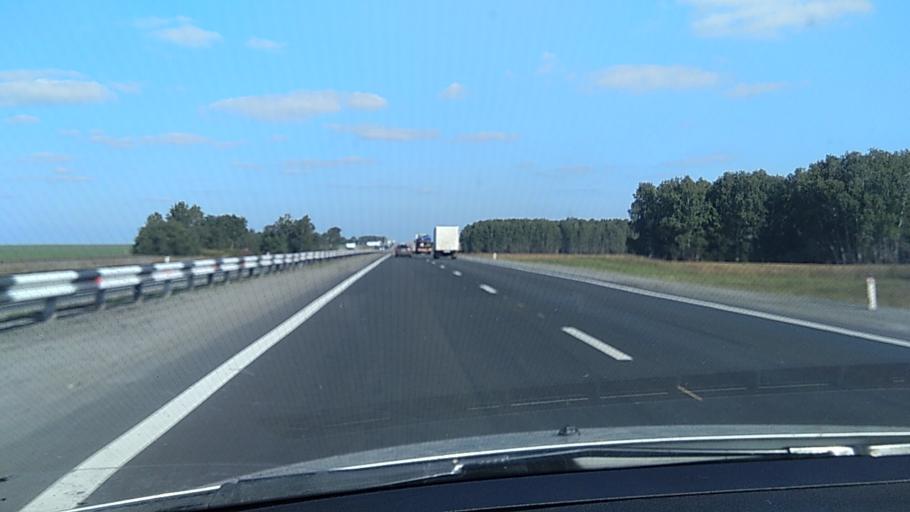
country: RU
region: Chelyabinsk
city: Timiryazevskiy
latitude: 54.9486
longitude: 60.8477
